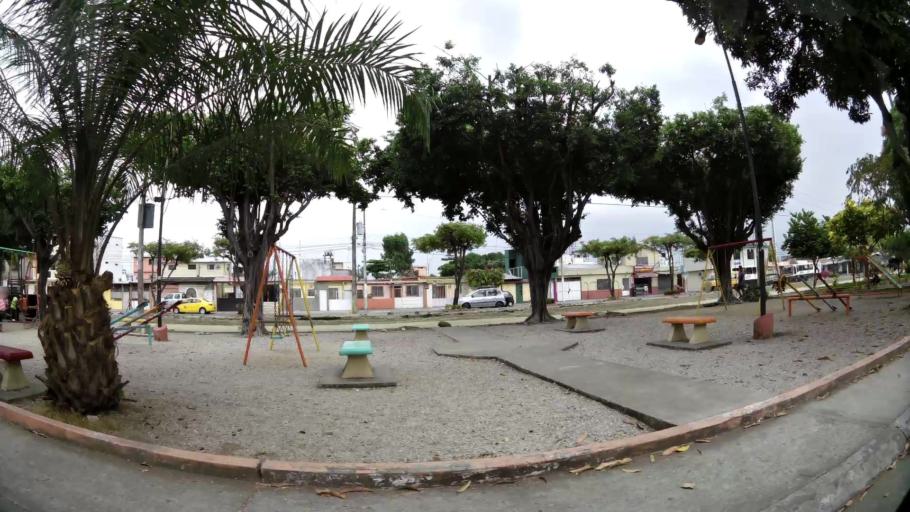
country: EC
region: Guayas
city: Eloy Alfaro
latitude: -2.1191
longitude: -79.8857
